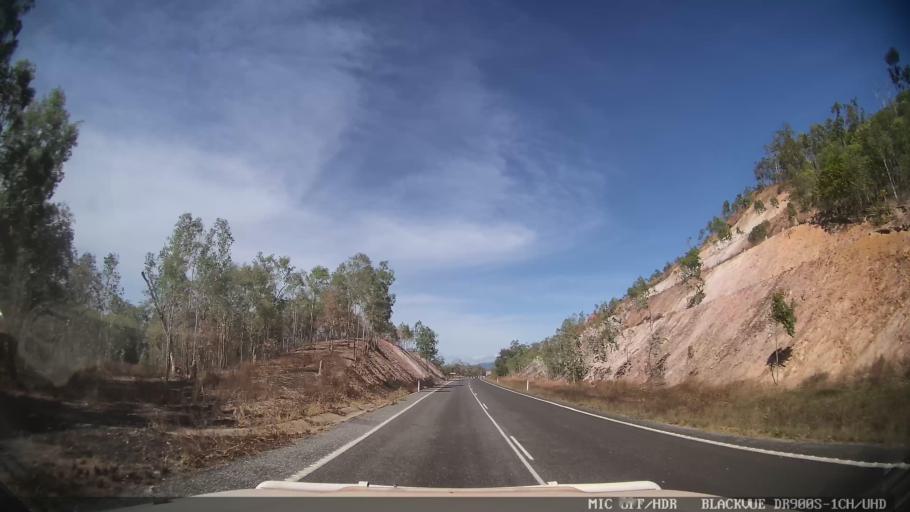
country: AU
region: Queensland
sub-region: Cook
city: Cooktown
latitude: -15.6915
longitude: 145.1170
